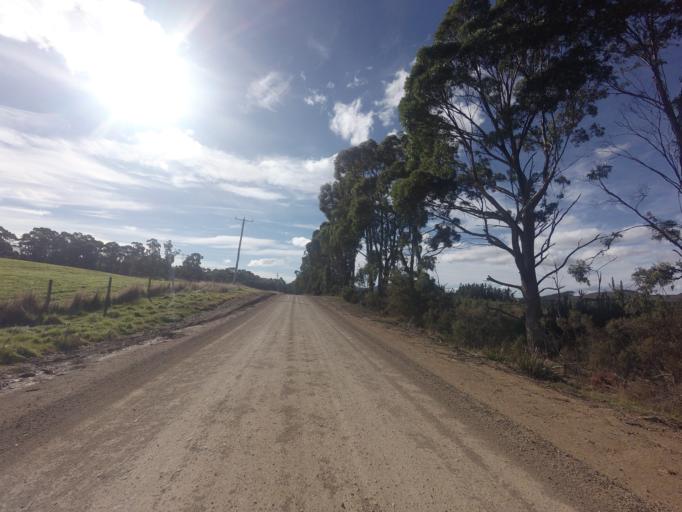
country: AU
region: Tasmania
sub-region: Clarence
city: Sandford
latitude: -43.1662
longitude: 147.7681
